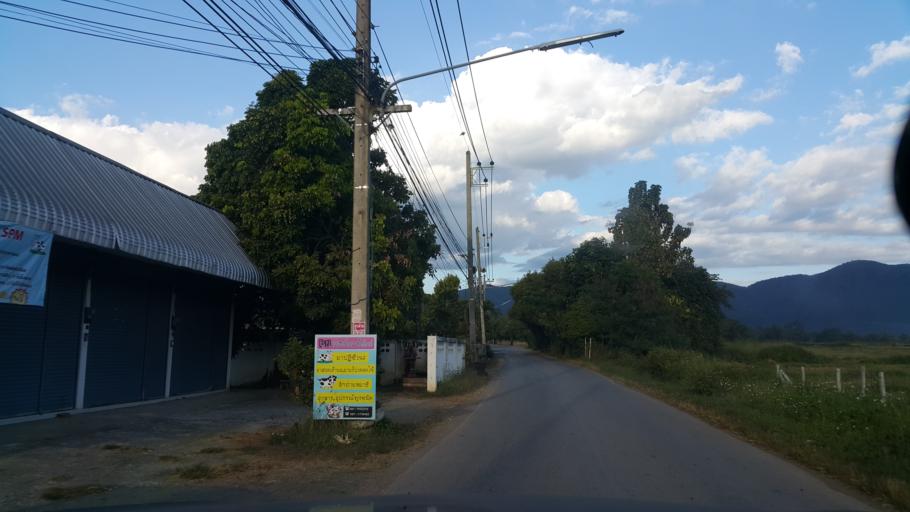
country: TH
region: Chiang Mai
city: Mae On
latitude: 18.7582
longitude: 99.2453
